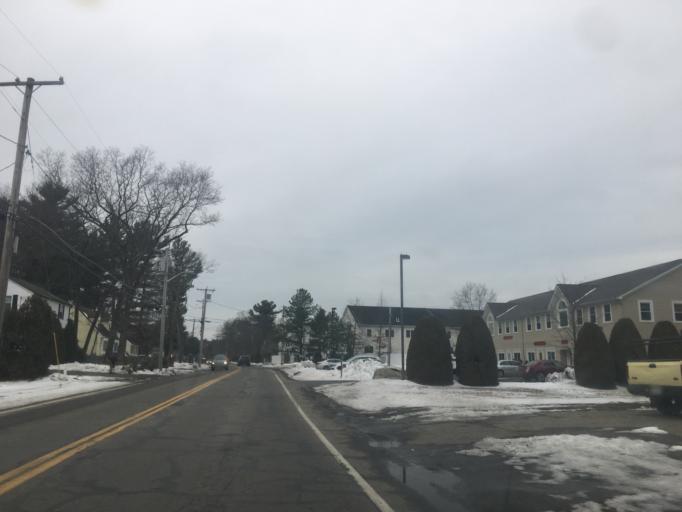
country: US
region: Massachusetts
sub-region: Middlesex County
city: Billerica
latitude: 42.5737
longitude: -71.2851
